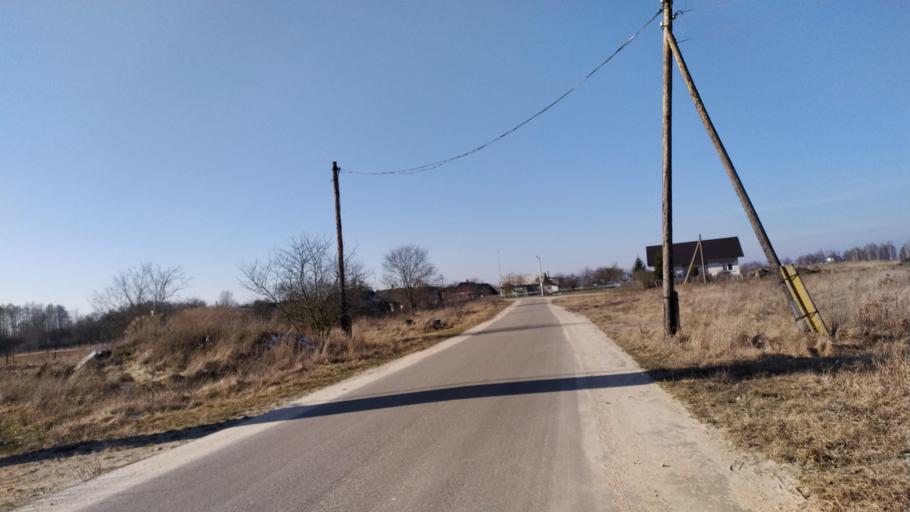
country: BY
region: Brest
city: Kamyanyets
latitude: 52.3854
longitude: 23.8029
